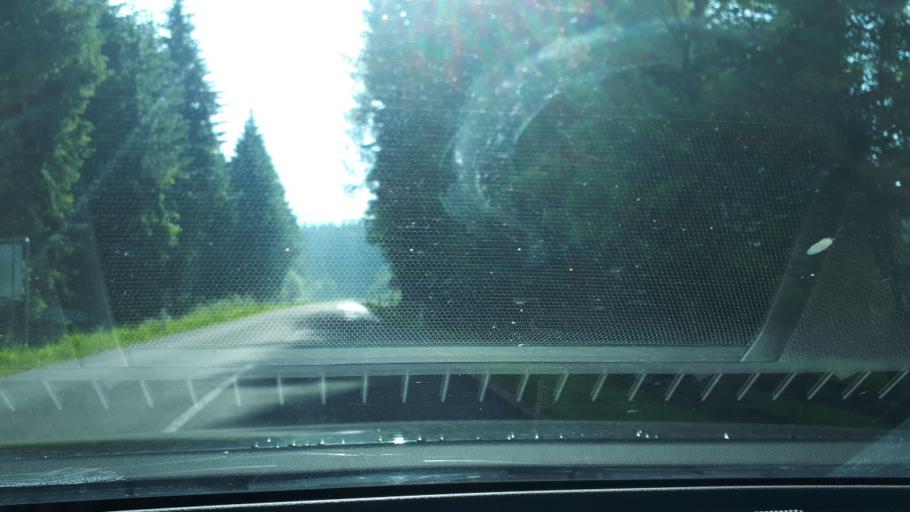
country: AT
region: Carinthia
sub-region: Politischer Bezirk Wolfsberg
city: Preitenegg
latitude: 46.9350
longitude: 14.9631
